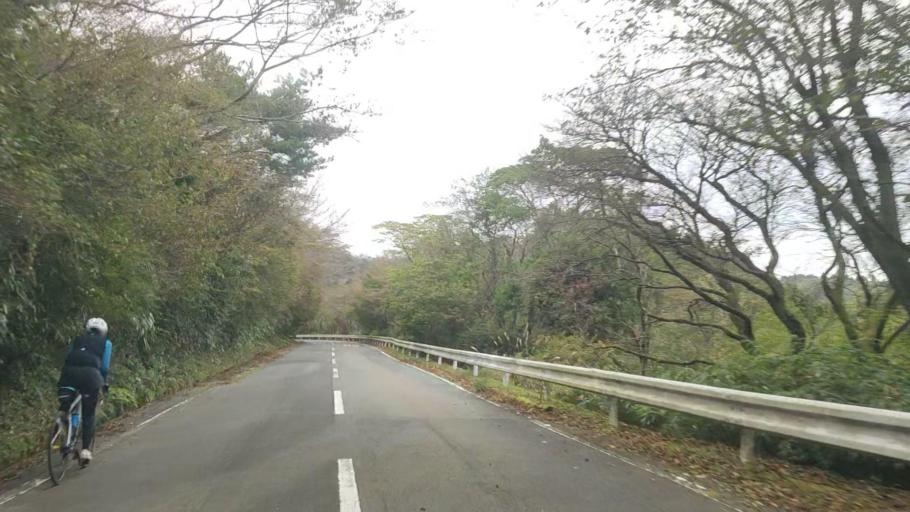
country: JP
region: Shizuoka
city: Heda
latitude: 34.9301
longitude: 138.8402
